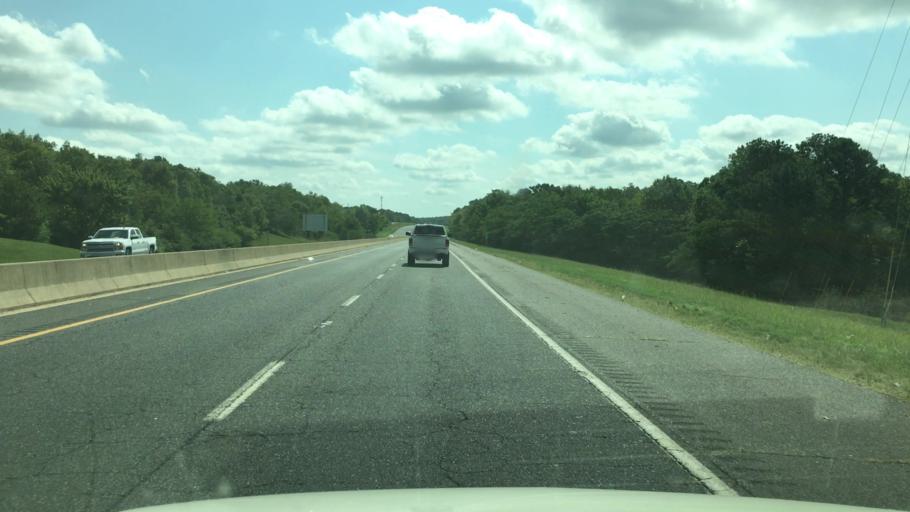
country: US
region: Arkansas
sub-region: Garland County
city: Rockwell
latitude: 34.4709
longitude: -93.1059
